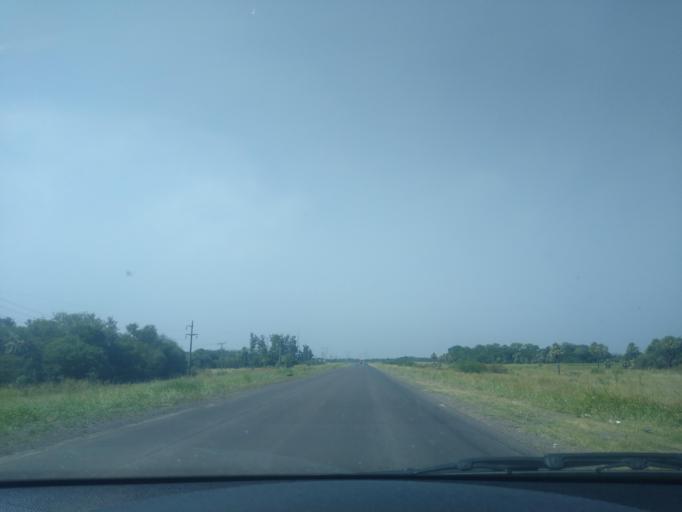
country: AR
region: Chaco
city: Fontana
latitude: -27.5711
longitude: -59.1547
